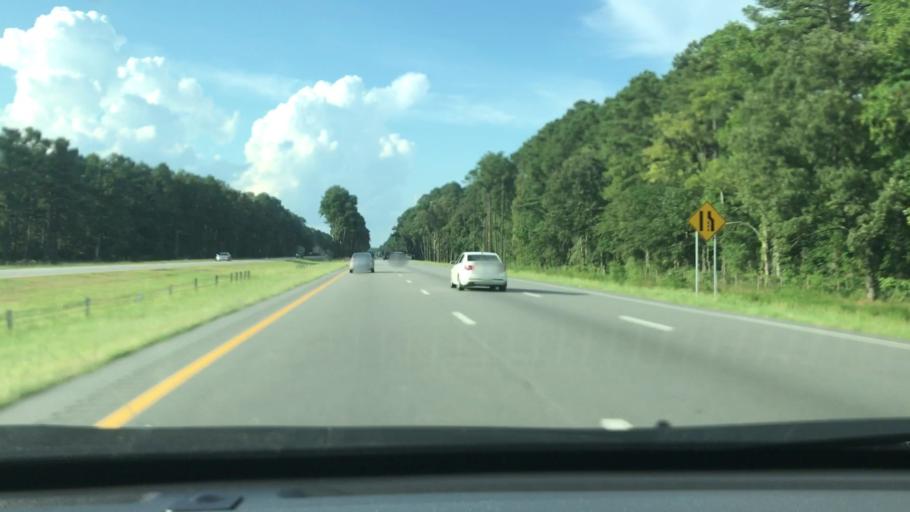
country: US
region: North Carolina
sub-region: Robeson County
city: Lumberton
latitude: 34.6756
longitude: -79.0048
